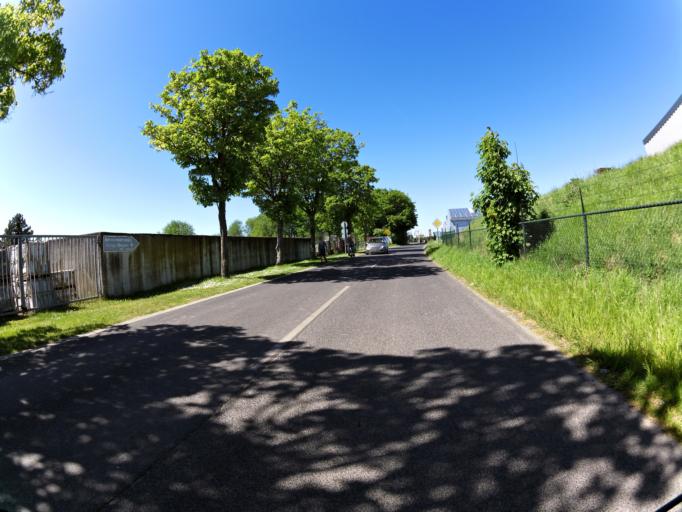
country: NL
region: Limburg
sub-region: Gemeente Sittard-Geleen
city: Sittard
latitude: 51.0184
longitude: 5.8863
